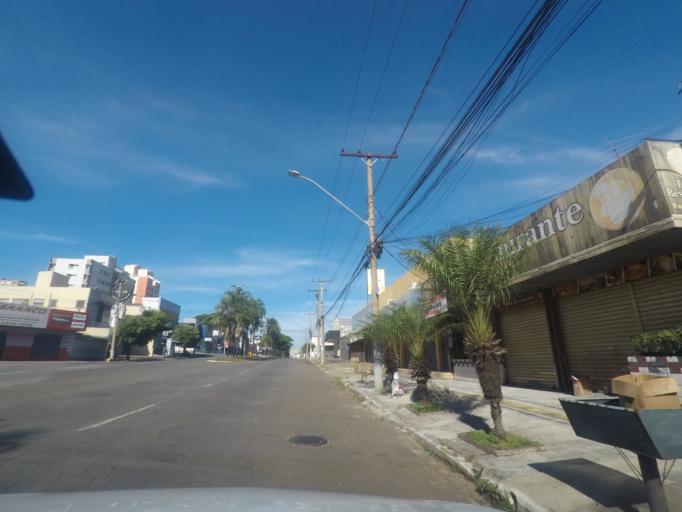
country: BR
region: Goias
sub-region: Goiania
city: Goiania
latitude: -16.6660
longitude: -49.2679
